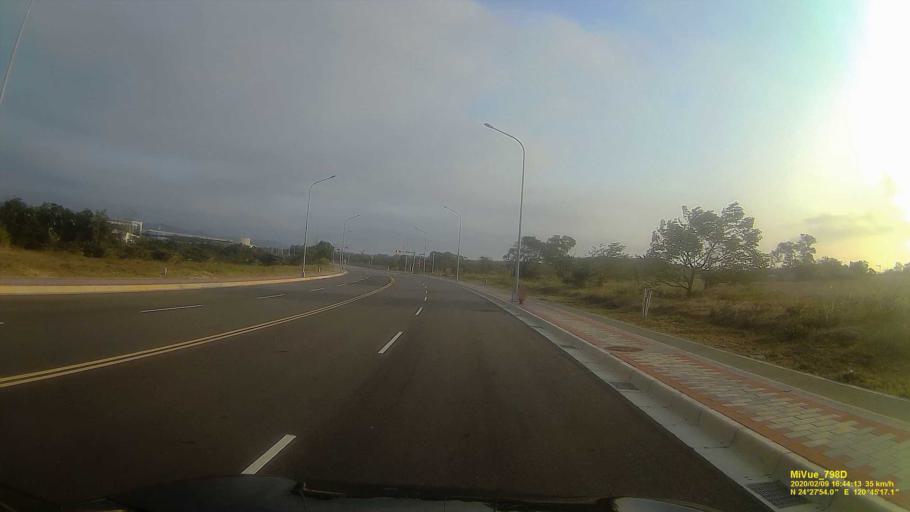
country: TW
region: Taiwan
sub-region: Miaoli
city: Miaoli
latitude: 24.4648
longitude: 120.7548
